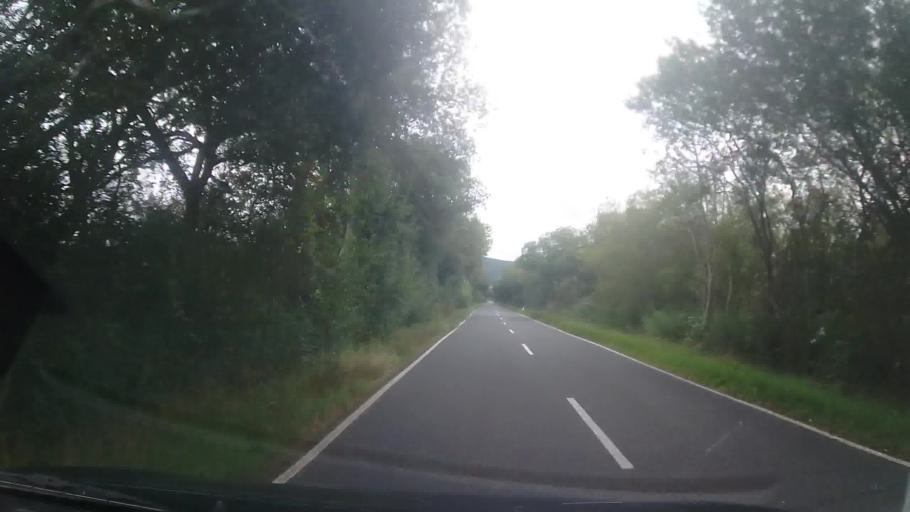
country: GB
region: Wales
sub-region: County of Ceredigion
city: Bow Street
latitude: 52.5142
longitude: -4.0085
